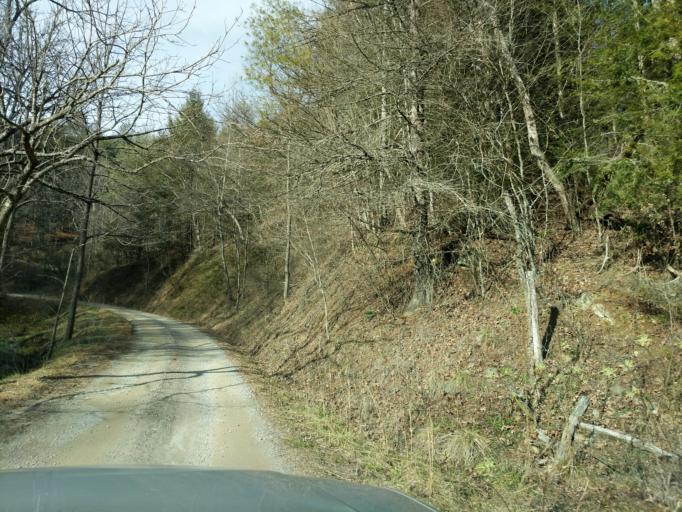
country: US
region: North Carolina
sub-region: Haywood County
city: Cove Creek
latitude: 35.6717
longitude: -83.0376
